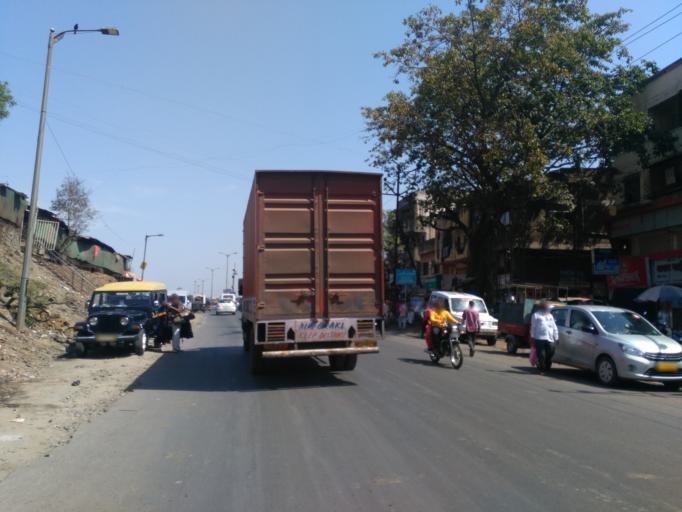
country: IN
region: Maharashtra
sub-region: Pune Division
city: Pune
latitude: 18.4452
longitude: 73.8593
